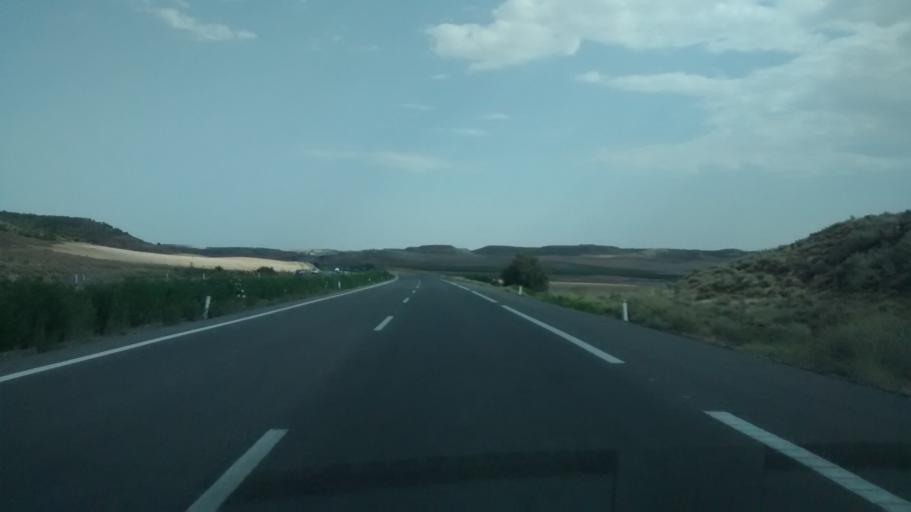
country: ES
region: Navarre
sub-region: Provincia de Navarra
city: Fontellas
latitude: 41.9892
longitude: -1.5737
